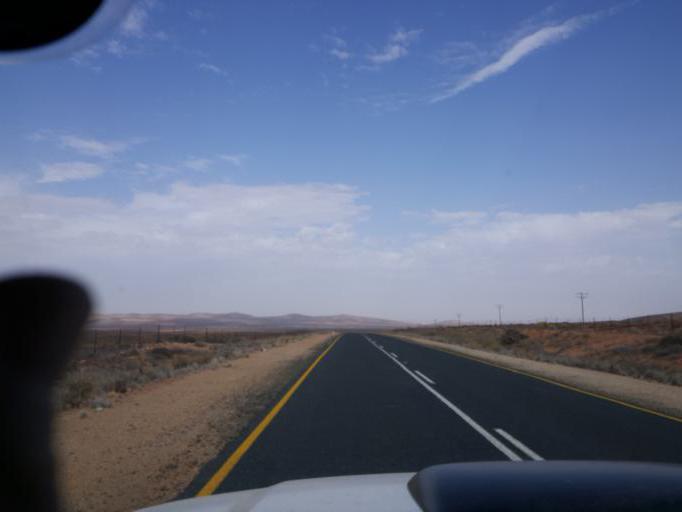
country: ZA
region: Northern Cape
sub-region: Namakwa District Municipality
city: Springbok
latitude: -29.2621
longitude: 17.4737
